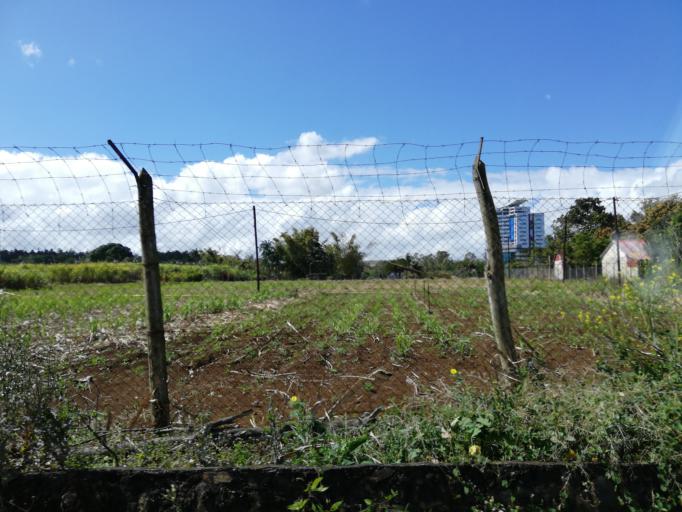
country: MU
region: Plaines Wilhems
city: Ebene
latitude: -20.2378
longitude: 57.4919
